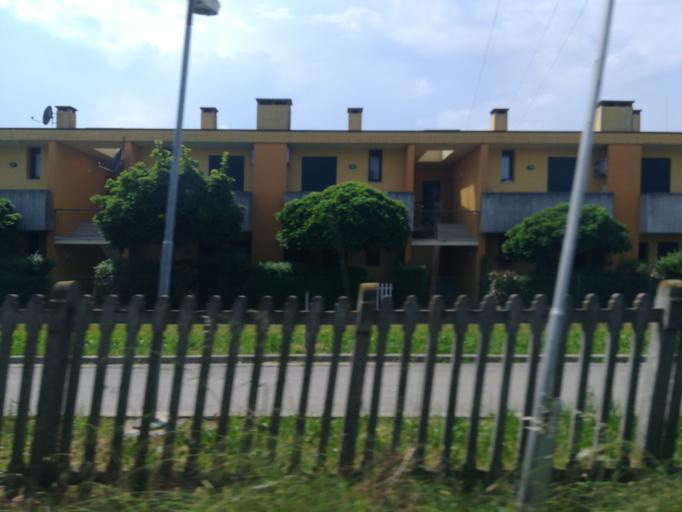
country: IT
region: Veneto
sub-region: Provincia di Vicenza
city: Monticello Conte Otto
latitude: 45.5920
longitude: 11.5696
